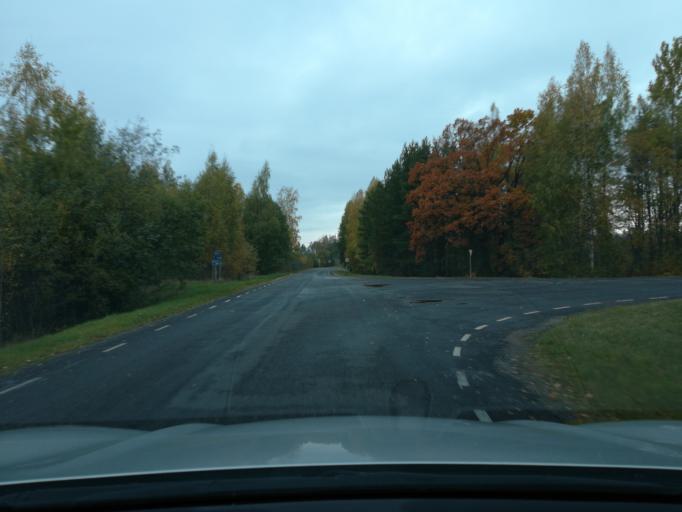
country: EE
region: Ida-Virumaa
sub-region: Johvi vald
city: Johvi
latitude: 59.0152
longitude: 27.4150
